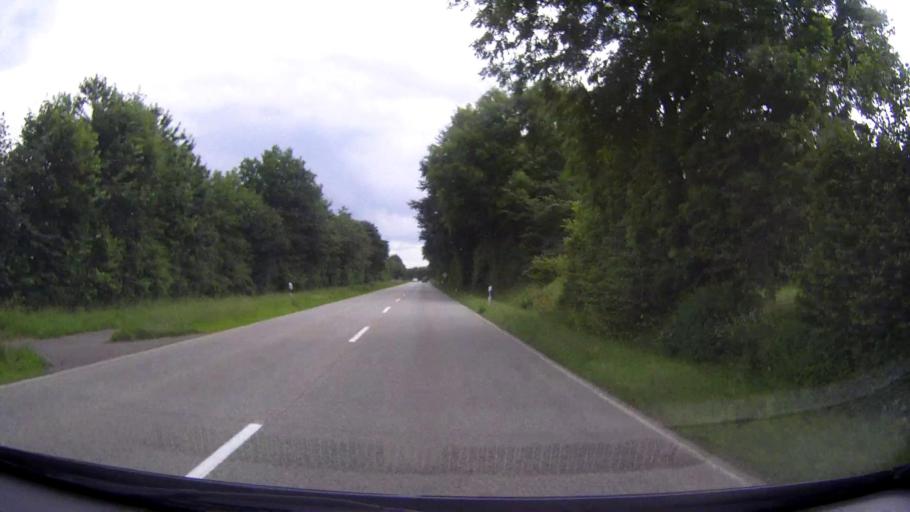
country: DE
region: Schleswig-Holstein
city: Seefeld
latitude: 54.0998
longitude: 9.4681
